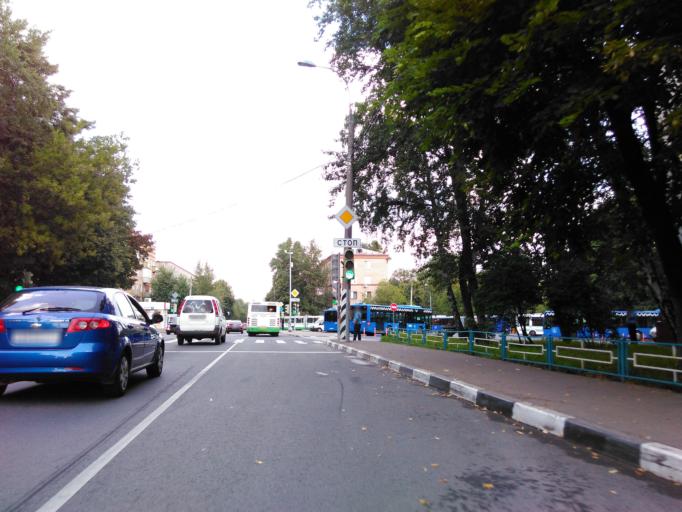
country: RU
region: Moscow
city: Kotlovka
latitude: 55.6723
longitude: 37.5947
